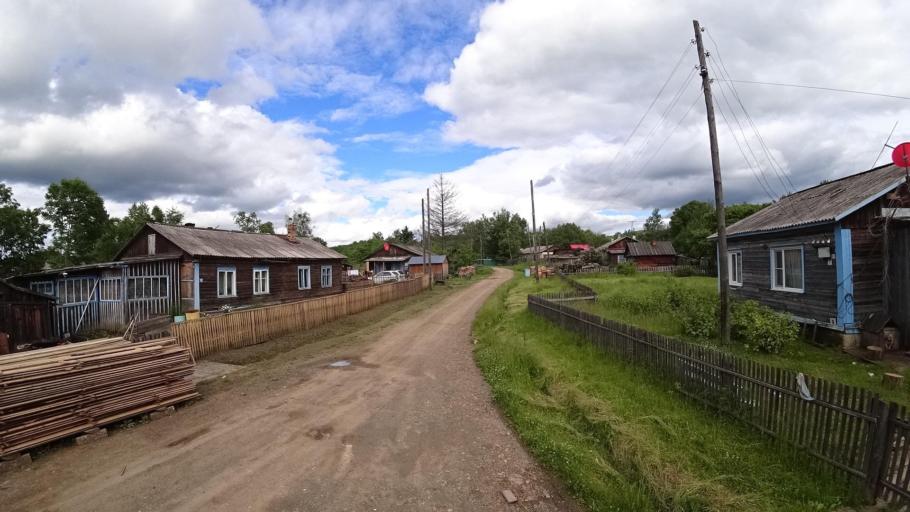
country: RU
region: Khabarovsk Krai
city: Litovko
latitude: 49.3663
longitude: 135.1693
